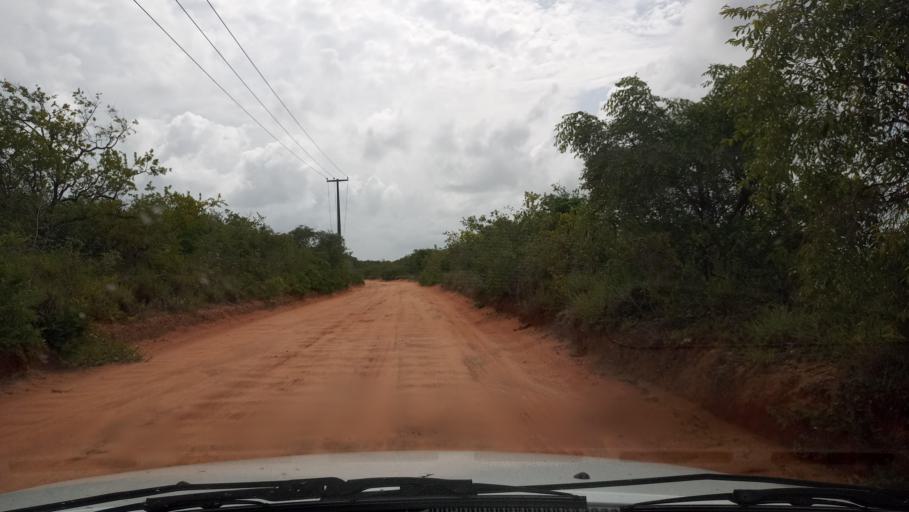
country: BR
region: Rio Grande do Norte
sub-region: Maxaranguape
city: Sao Miguel
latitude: -5.4832
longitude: -35.3221
